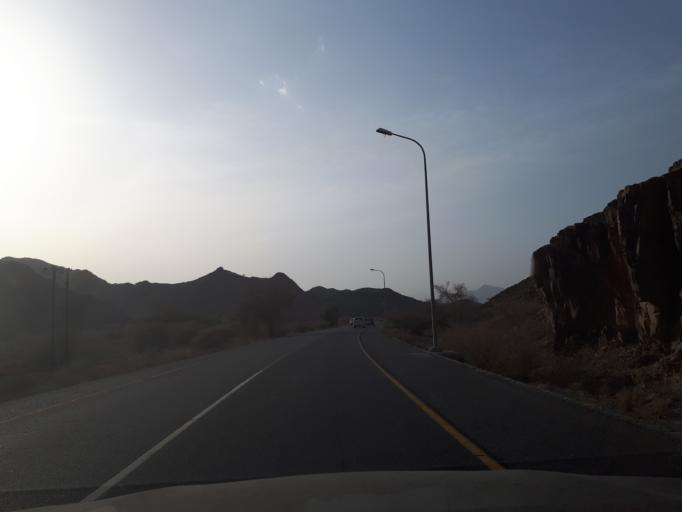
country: OM
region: Muhafazat ad Dakhiliyah
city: Sufalat Sama'il
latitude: 23.1614
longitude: 58.1055
